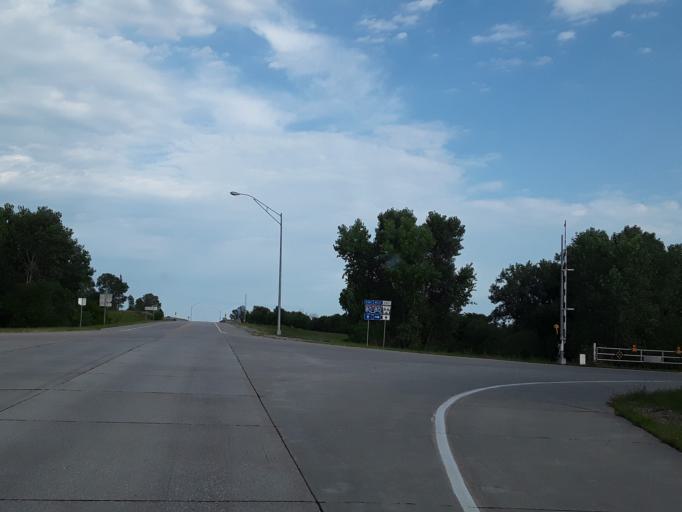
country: US
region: Nebraska
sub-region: Saunders County
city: Ashland
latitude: 41.0133
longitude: -96.3102
